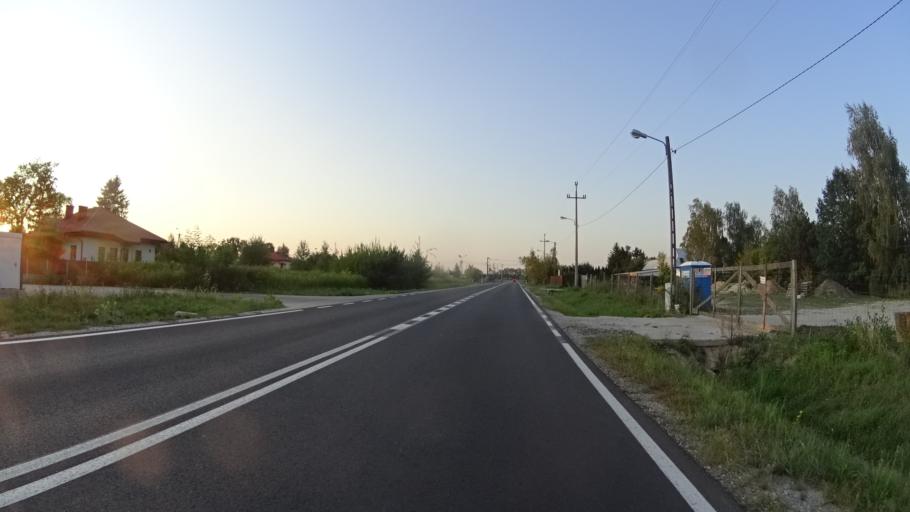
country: PL
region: Masovian Voivodeship
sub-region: Powiat warszawski zachodni
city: Truskaw
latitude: 52.2504
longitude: 20.7413
